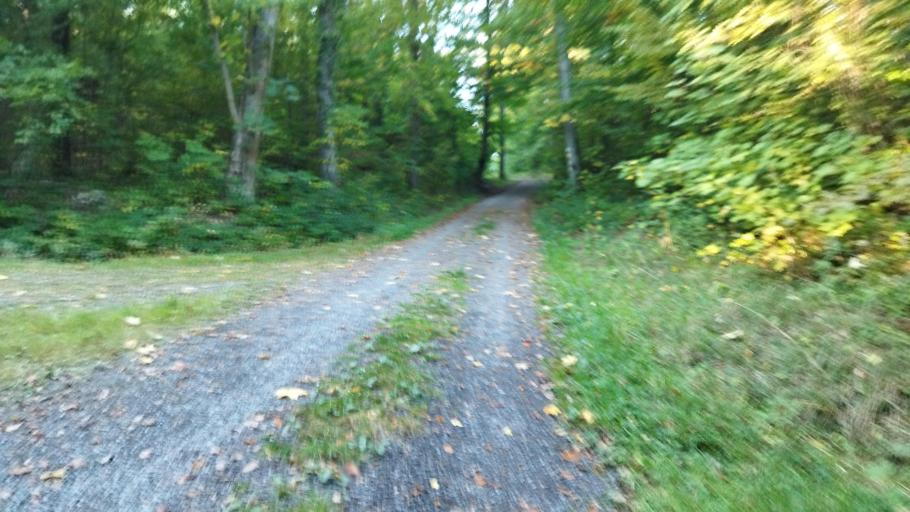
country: DE
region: Baden-Wuerttemberg
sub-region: Regierungsbezirk Stuttgart
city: Freudental
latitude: 49.0089
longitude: 9.0342
